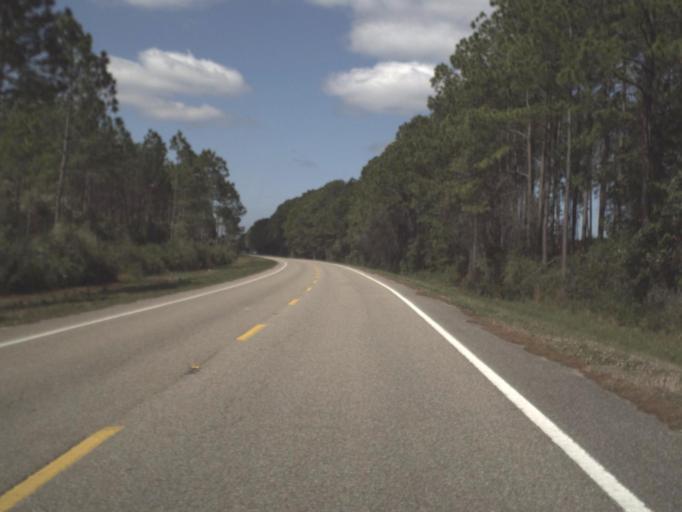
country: US
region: Florida
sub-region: Gulf County
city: Port Saint Joe
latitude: 29.7352
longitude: -85.1542
